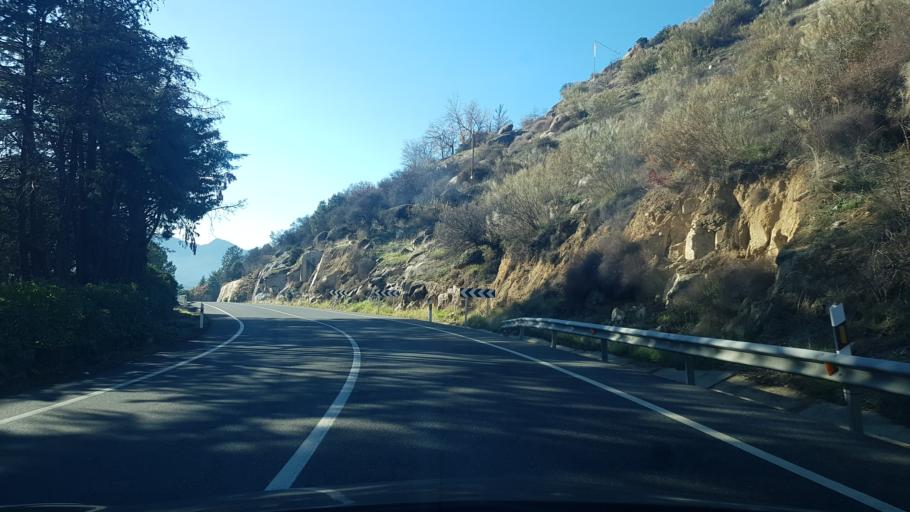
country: ES
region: Castille and Leon
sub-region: Provincia de Avila
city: El Tiemblo
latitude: 40.4294
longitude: -4.5456
